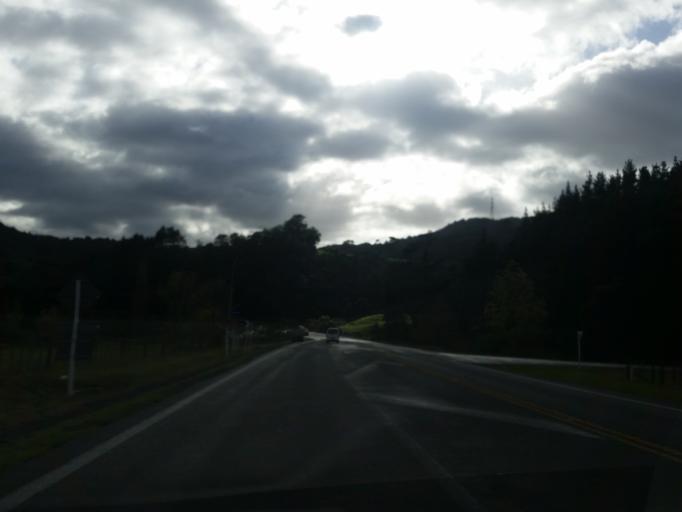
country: NZ
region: Waikato
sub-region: Hauraki District
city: Paeroa
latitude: -37.4084
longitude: 175.7062
